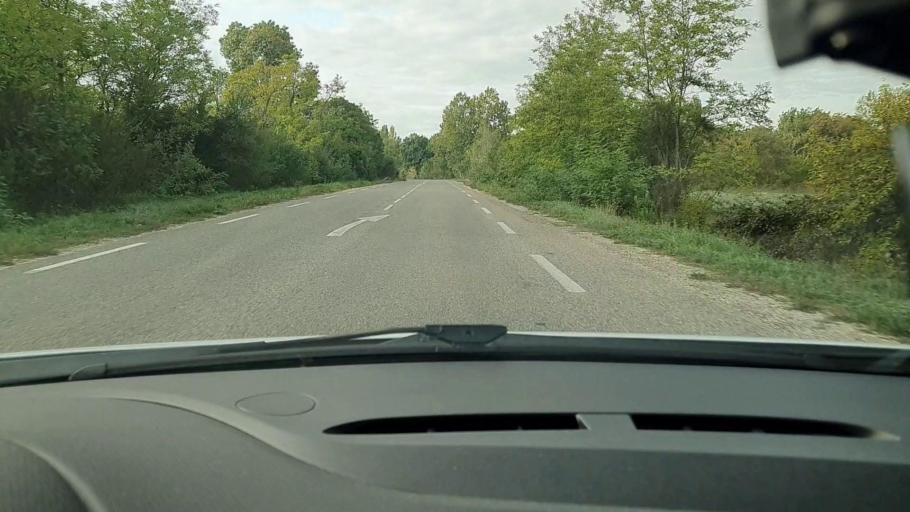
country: FR
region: Languedoc-Roussillon
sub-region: Departement du Gard
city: Saint-Ambroix
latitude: 44.2010
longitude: 4.2452
